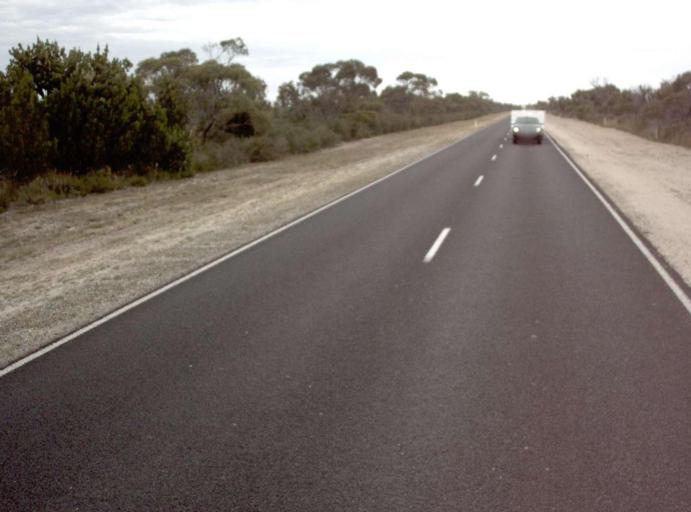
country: AU
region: Victoria
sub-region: East Gippsland
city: Bairnsdale
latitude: -38.1193
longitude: 147.4574
